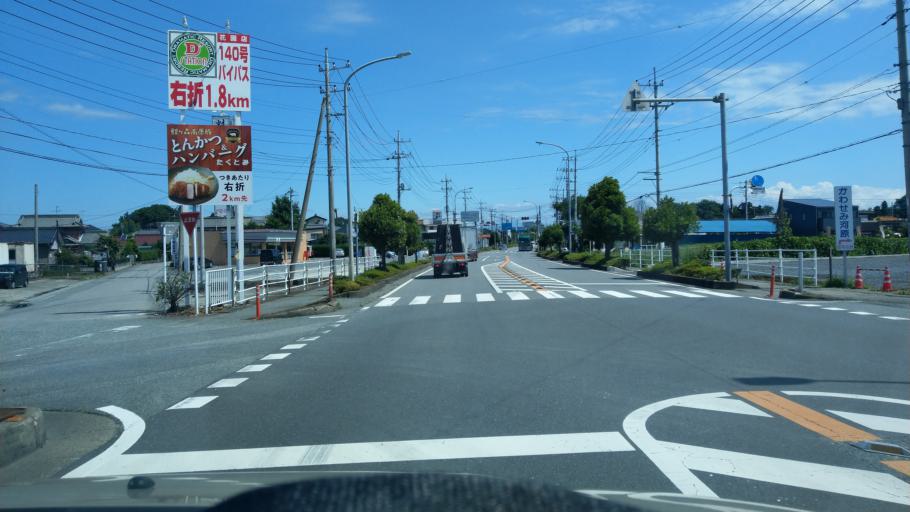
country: JP
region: Saitama
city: Yorii
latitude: 36.1164
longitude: 139.2106
